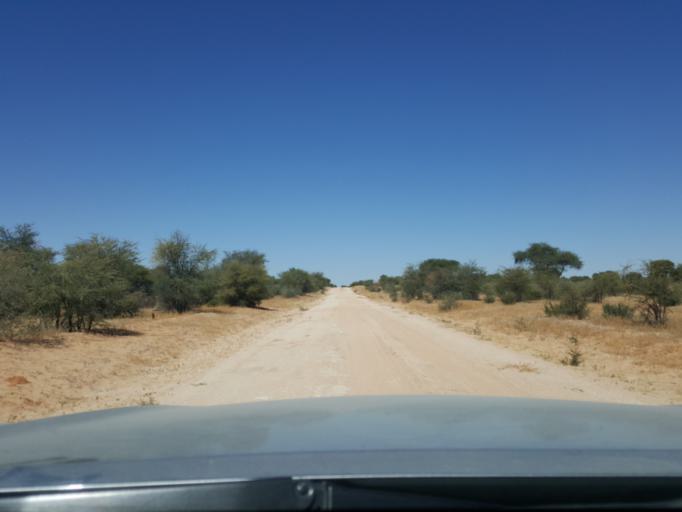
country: BW
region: Kgalagadi
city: Hukuntsi
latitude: -23.9890
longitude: 21.2099
